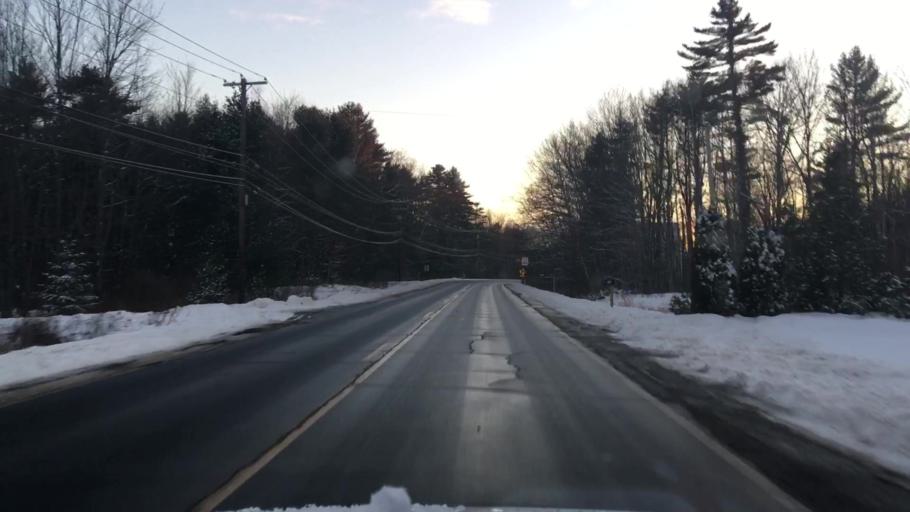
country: US
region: Maine
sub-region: Cumberland County
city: Brunswick
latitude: 43.9437
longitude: -69.9294
